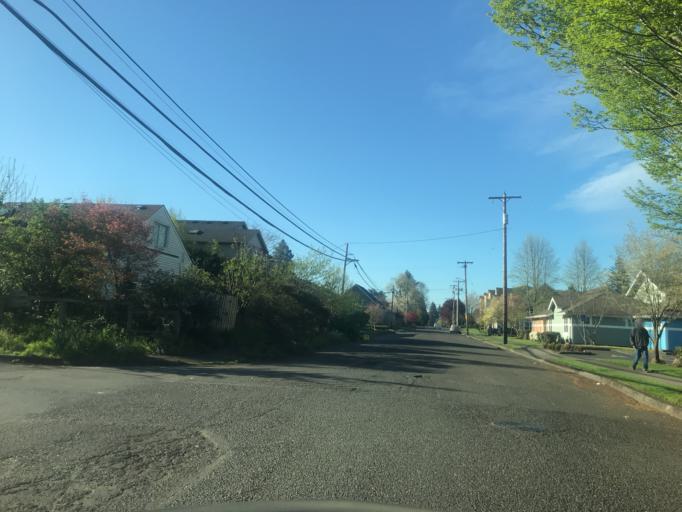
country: US
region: Oregon
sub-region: Multnomah County
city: Lents
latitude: 45.4963
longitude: -122.5809
